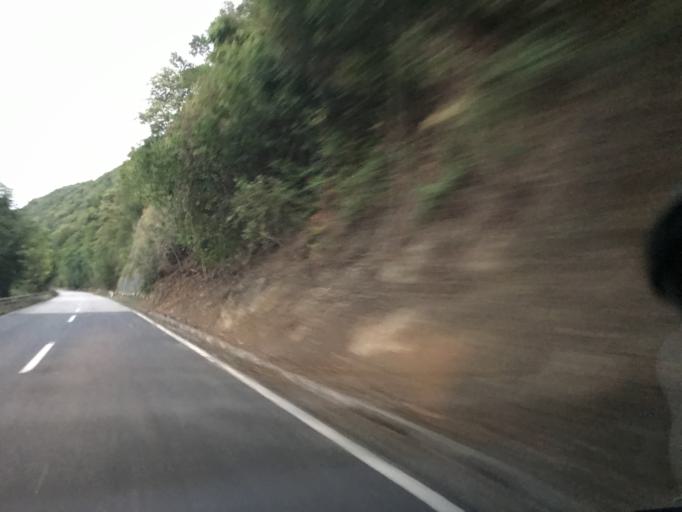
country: RO
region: Caras-Severin
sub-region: Comuna Berzasca
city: Liubcova
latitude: 44.6448
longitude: 21.8177
